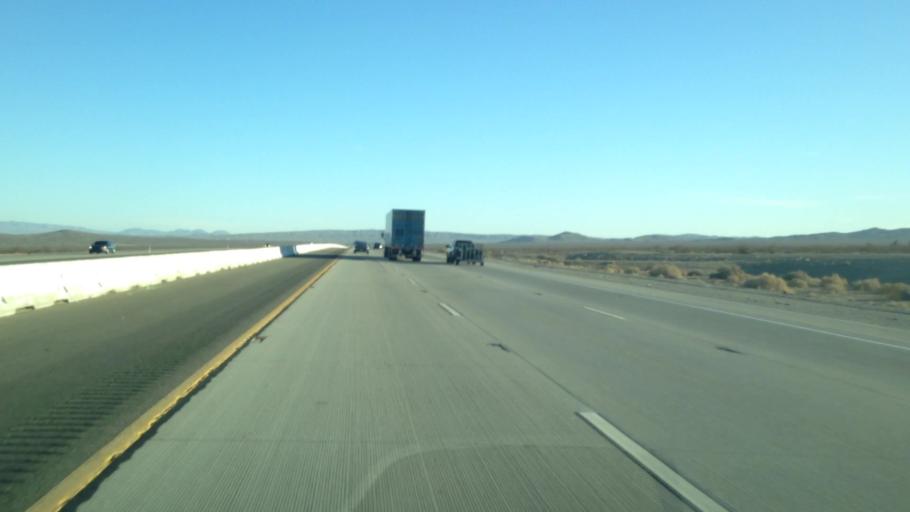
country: US
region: California
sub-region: San Bernardino County
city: Lenwood
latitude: 34.7779
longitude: -117.1357
